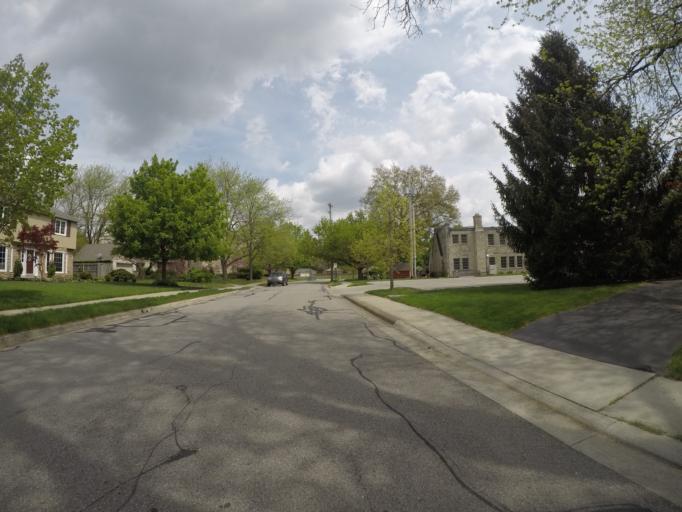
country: US
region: Ohio
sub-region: Franklin County
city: Upper Arlington
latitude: 39.9975
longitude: -83.0529
